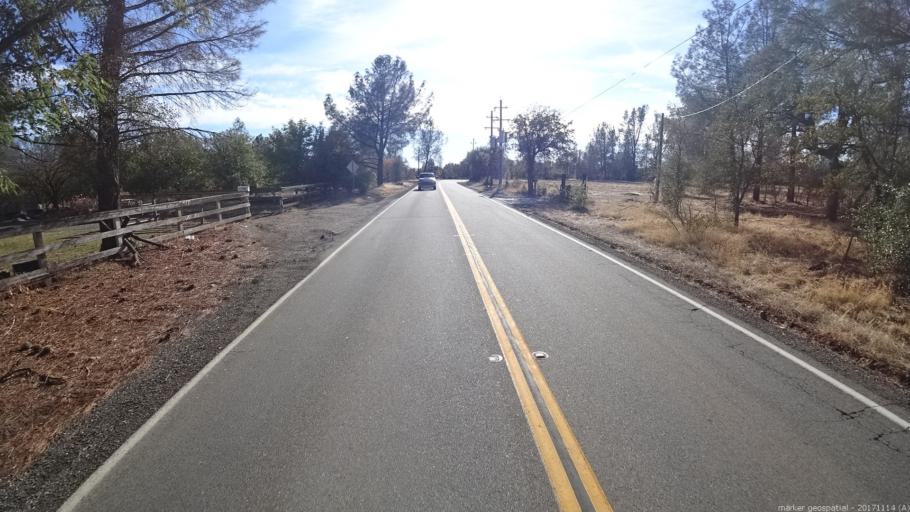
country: US
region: California
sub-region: Shasta County
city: Anderson
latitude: 40.4511
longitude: -122.4024
